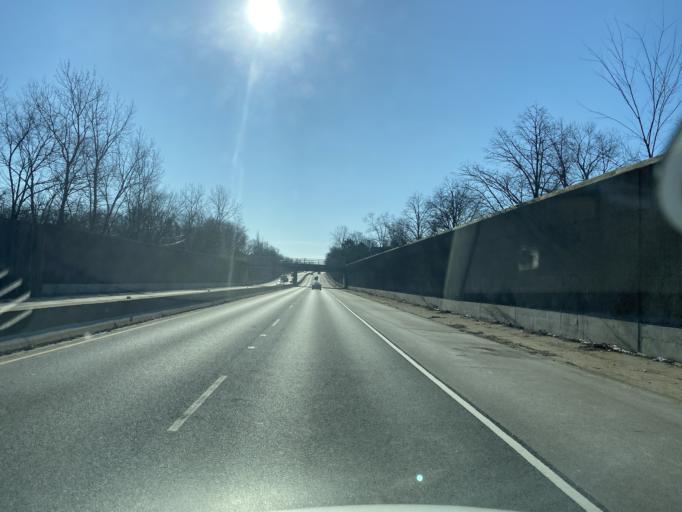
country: US
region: Illinois
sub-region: DuPage County
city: Hinsdale
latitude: 41.8048
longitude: -87.9467
